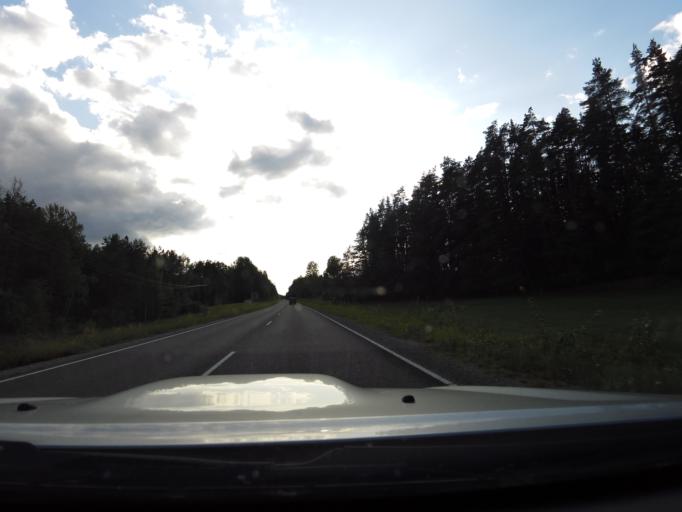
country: LT
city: Juodupe
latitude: 56.2056
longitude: 25.5954
